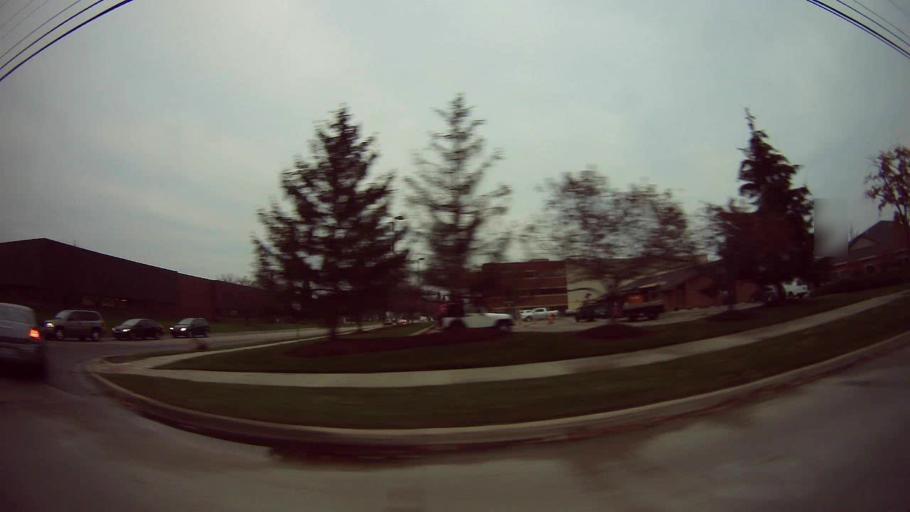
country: US
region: Michigan
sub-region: Oakland County
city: Clawson
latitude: 42.5493
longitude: -83.1120
